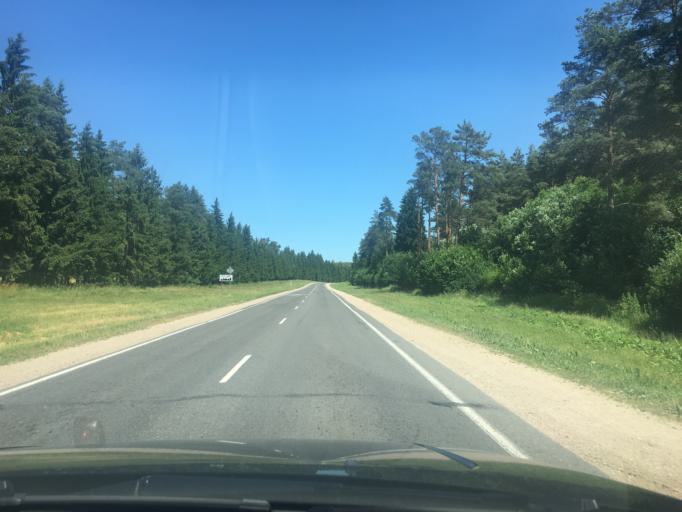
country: BY
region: Grodnenskaya
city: Hal'shany
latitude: 54.2169
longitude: 25.9701
